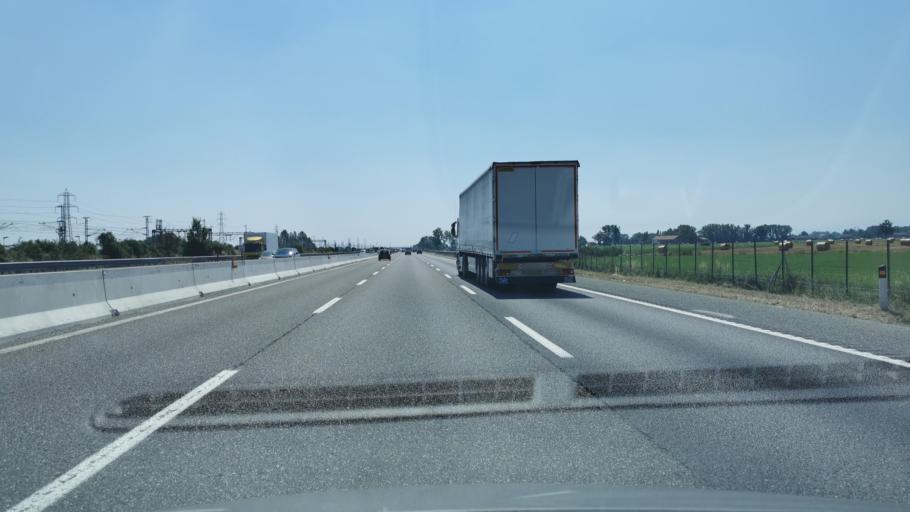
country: IT
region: Emilia-Romagna
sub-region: Provincia di Piacenza
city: Alseno
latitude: 44.9153
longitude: 10.0092
